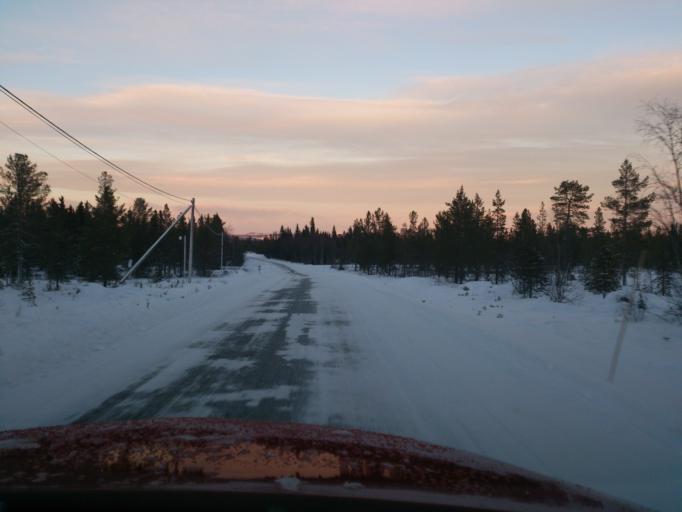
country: SE
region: Jaemtland
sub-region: Harjedalens Kommun
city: Sveg
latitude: 62.3218
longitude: 13.4193
